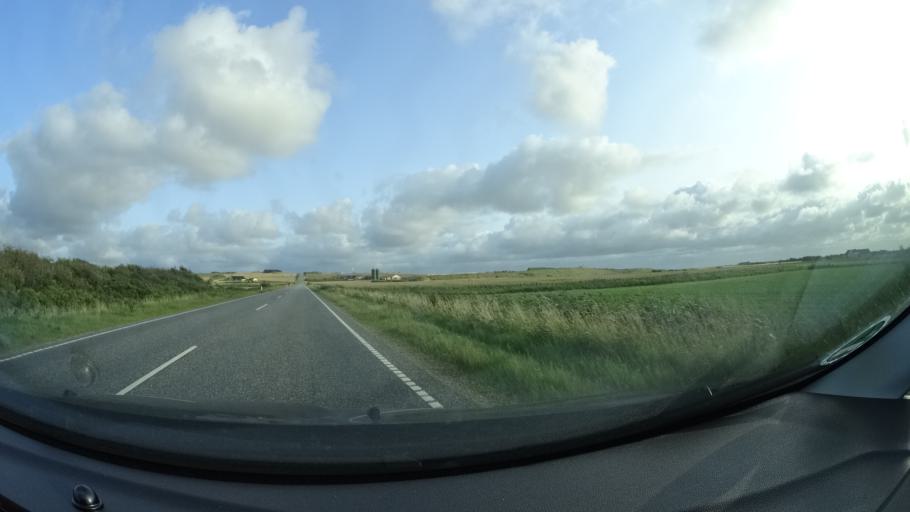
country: DK
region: Central Jutland
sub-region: Lemvig Kommune
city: Harboore
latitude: 56.5983
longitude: 8.1871
